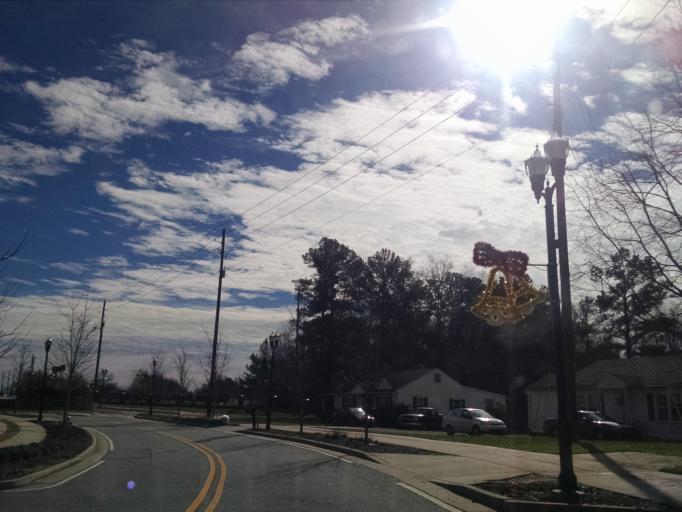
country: US
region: Georgia
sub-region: Gwinnett County
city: Sugar Hill
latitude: 34.1092
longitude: -84.0392
